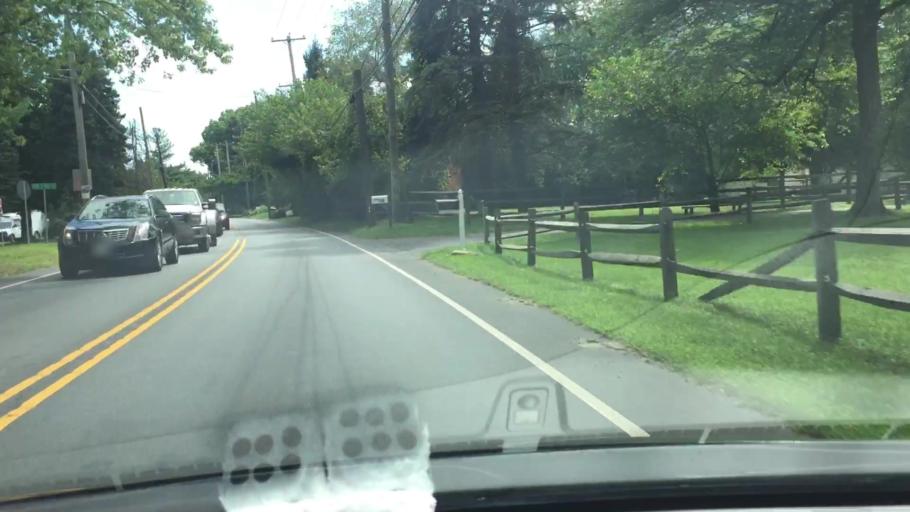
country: US
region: Pennsylvania
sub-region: Delaware County
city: Lima
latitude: 39.9091
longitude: -75.4401
